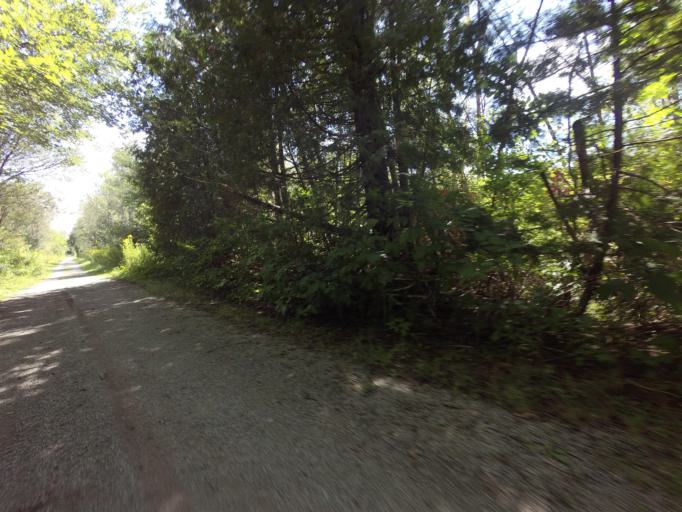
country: CA
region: Ontario
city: Orangeville
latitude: 43.7817
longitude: -80.1297
